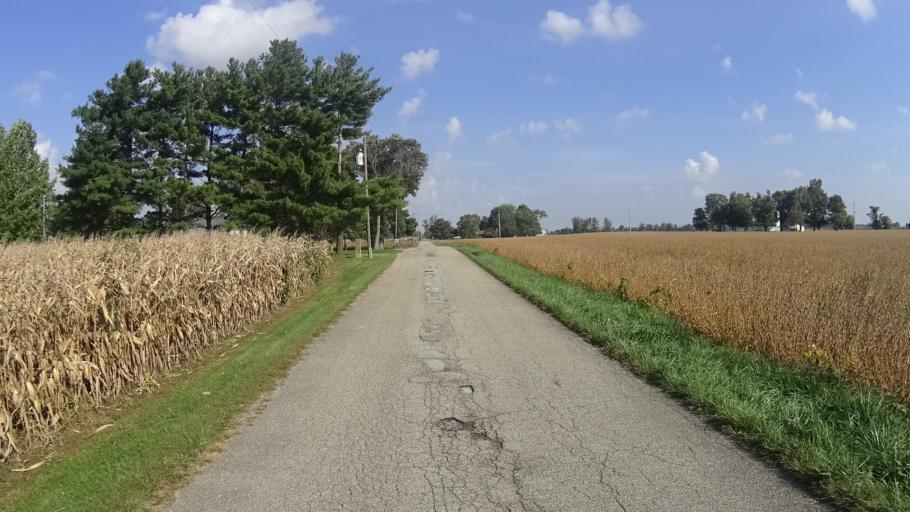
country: US
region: Indiana
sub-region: Madison County
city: Ingalls
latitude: 40.0136
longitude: -85.8243
